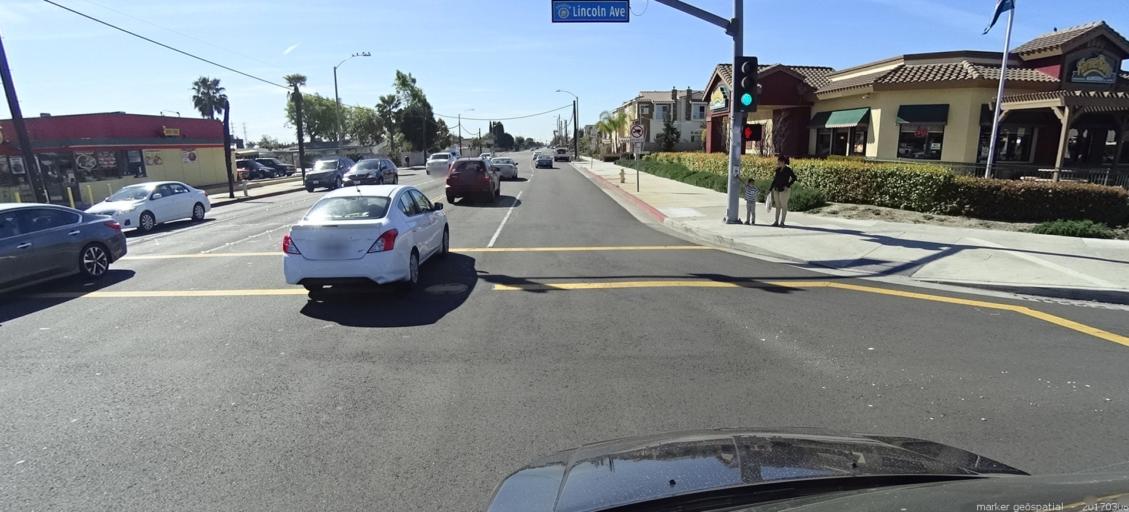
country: US
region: California
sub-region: Orange County
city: Stanton
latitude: 33.8321
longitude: -117.9848
